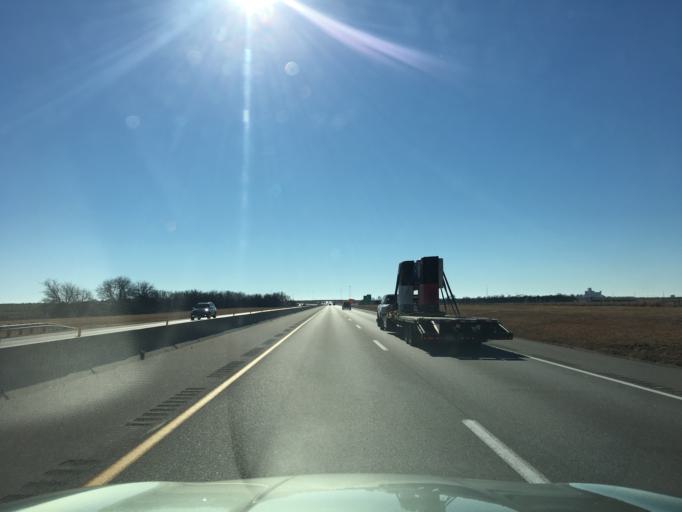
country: US
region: Kansas
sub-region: Sumner County
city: Wellington
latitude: 37.2907
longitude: -97.3403
